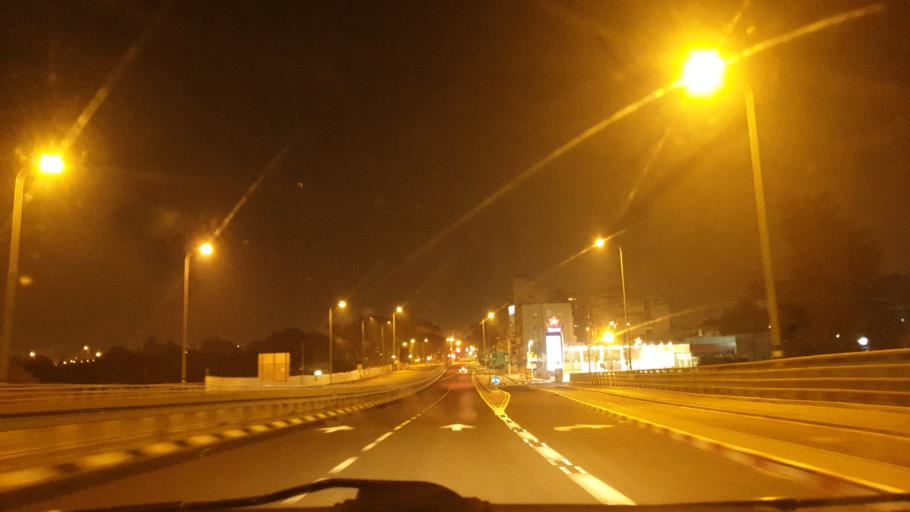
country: IL
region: Central District
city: Ramla
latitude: 31.9411
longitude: 34.8651
